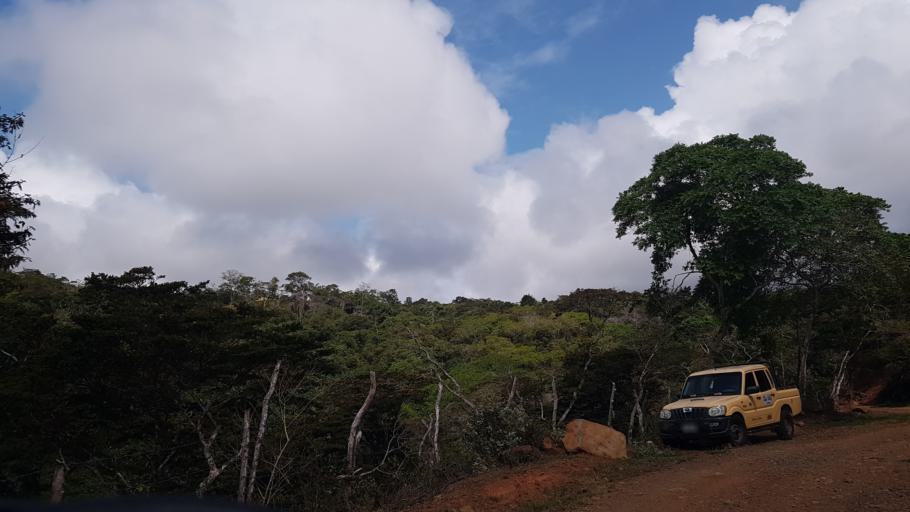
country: CO
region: Valle del Cauca
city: Yumbo
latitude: 3.6548
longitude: -76.5189
